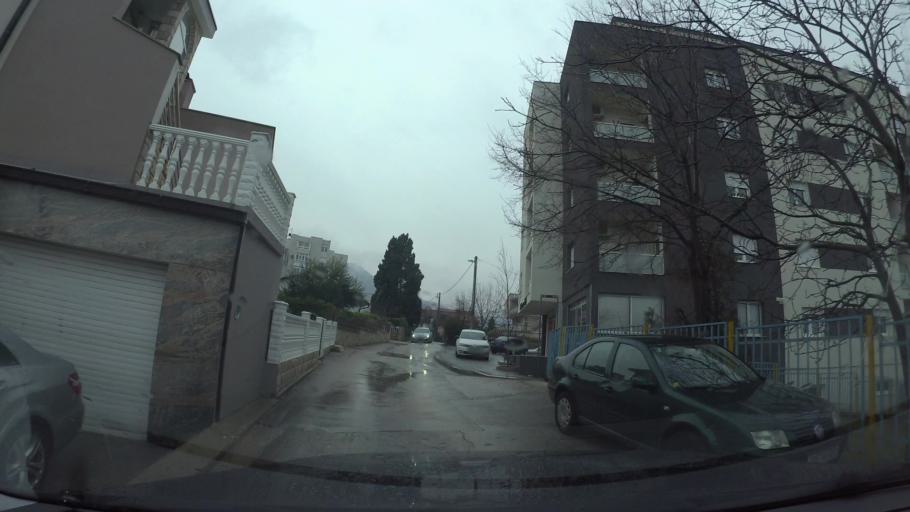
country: BA
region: Federation of Bosnia and Herzegovina
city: Cim
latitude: 43.3476
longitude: 17.7926
